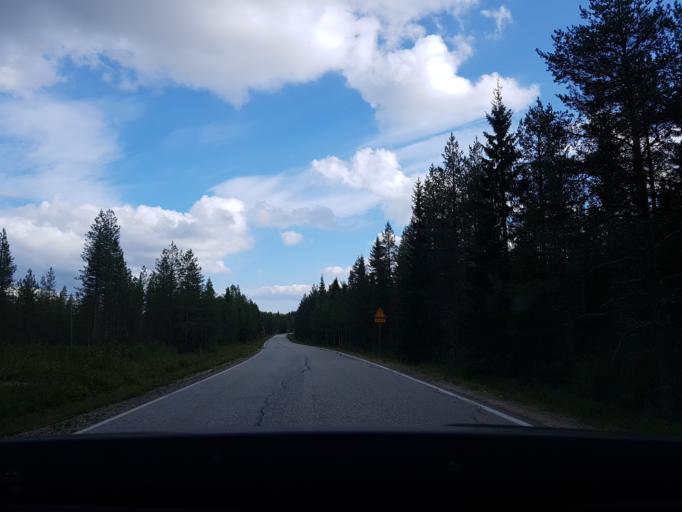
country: FI
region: Kainuu
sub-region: Kehys-Kainuu
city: Kuhmo
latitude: 64.6292
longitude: 29.6920
